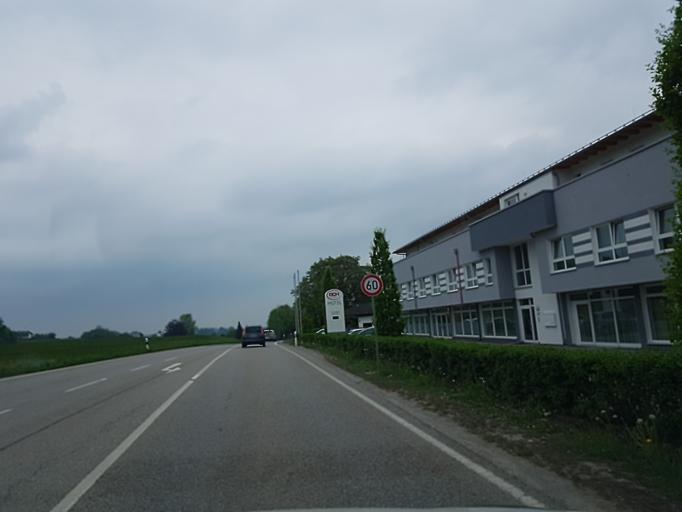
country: DE
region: Bavaria
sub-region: Upper Bavaria
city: Ebersberg
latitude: 48.0944
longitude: 11.9650
